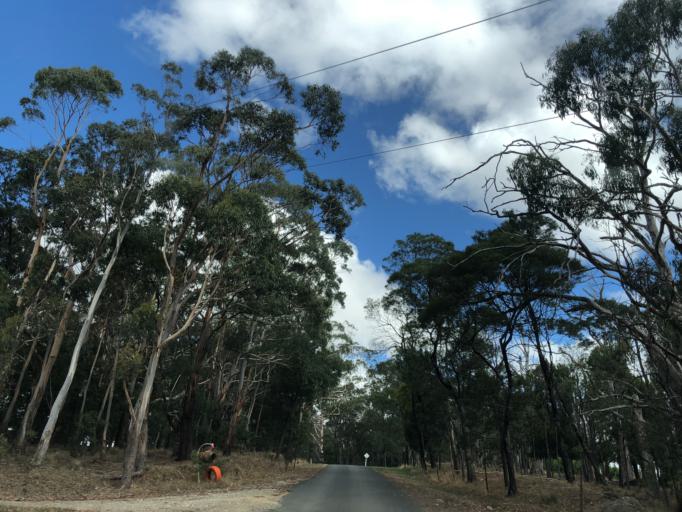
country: AU
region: Victoria
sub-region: Moorabool
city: Bacchus Marsh
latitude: -37.5540
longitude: 144.3493
